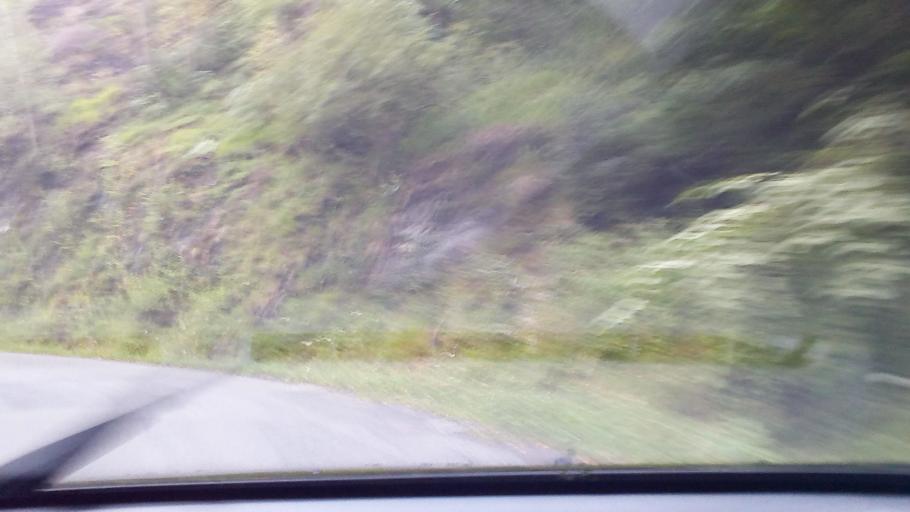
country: FR
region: Midi-Pyrenees
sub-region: Departement des Hautes-Pyrenees
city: Cauterets
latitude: 42.9479
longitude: -0.2127
